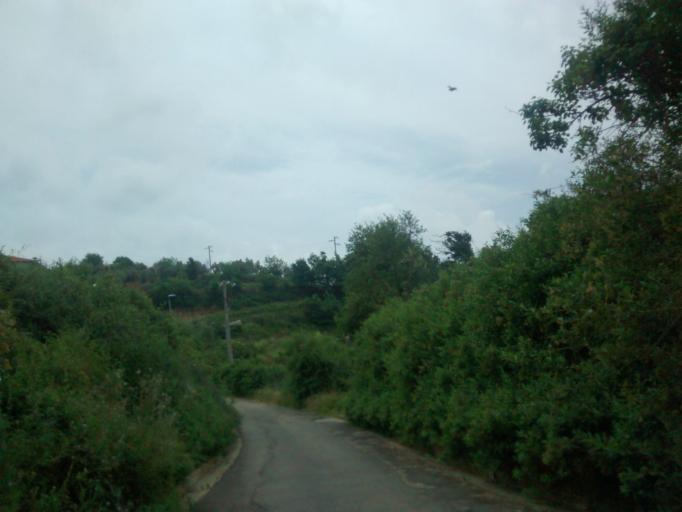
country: IT
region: Calabria
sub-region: Provincia di Catanzaro
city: Cortale
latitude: 38.8872
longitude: 16.4070
